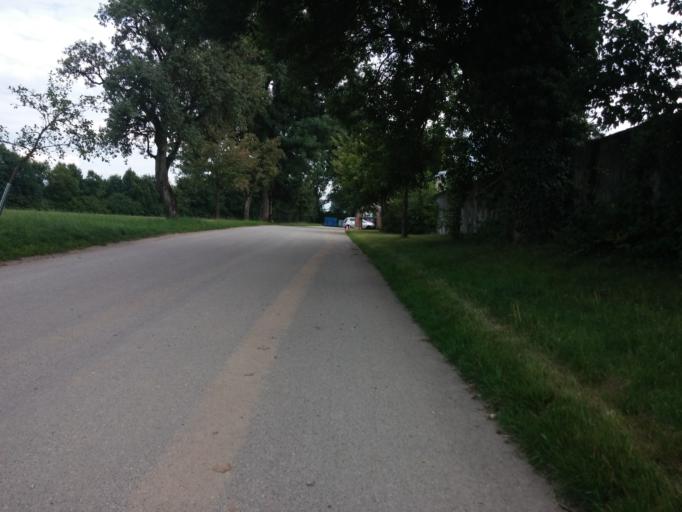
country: DE
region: Baden-Wuerttemberg
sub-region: Tuebingen Region
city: Aitrach
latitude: 47.9360
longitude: 10.0960
